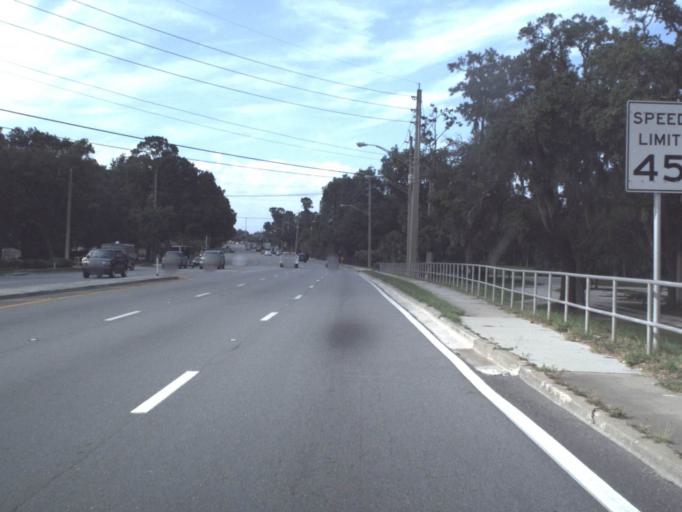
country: US
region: Florida
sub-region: Clay County
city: Orange Park
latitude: 30.2157
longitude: -81.6176
